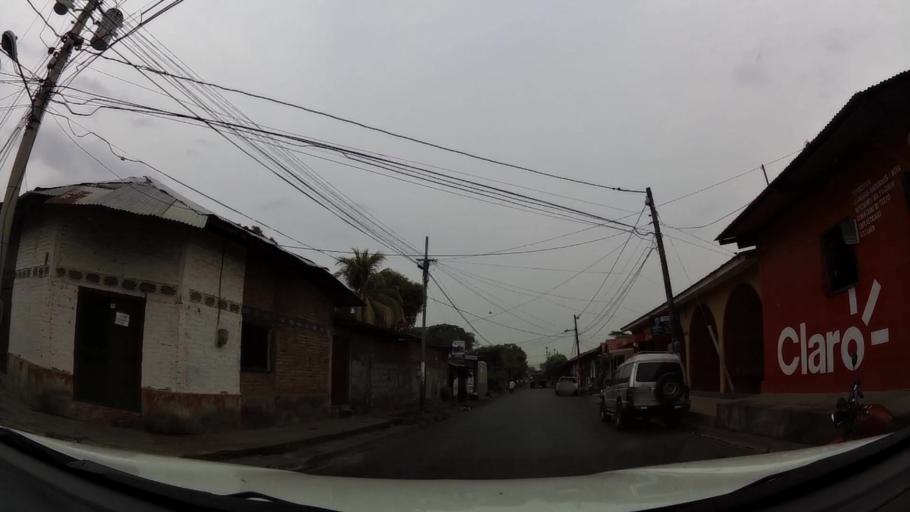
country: NI
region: Leon
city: Leon
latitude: 12.4466
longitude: -86.8769
